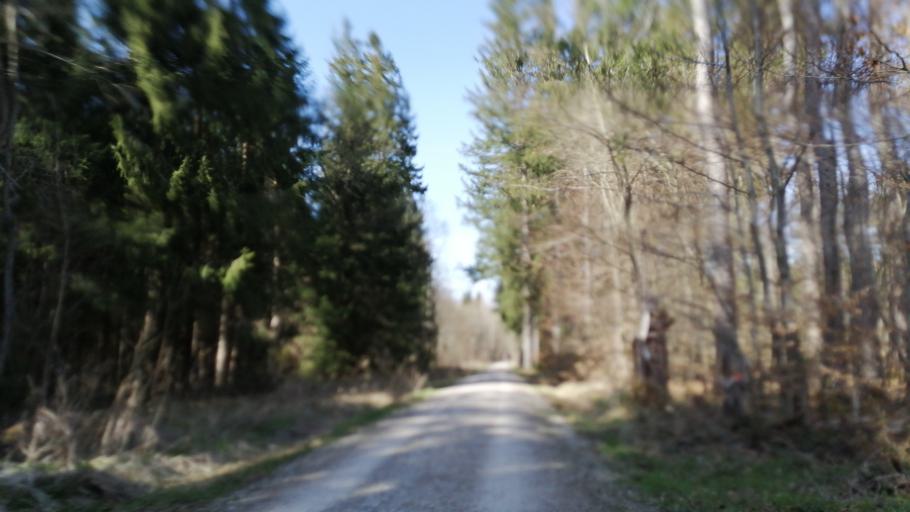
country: DE
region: Bavaria
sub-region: Upper Bavaria
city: Oberhaching
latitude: 48.0011
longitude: 11.6272
